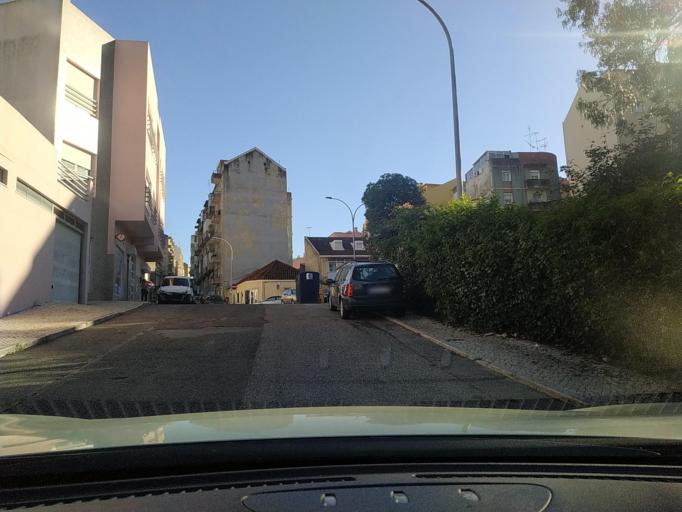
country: PT
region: Lisbon
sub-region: Odivelas
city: Pontinha
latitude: 38.7700
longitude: -9.2146
